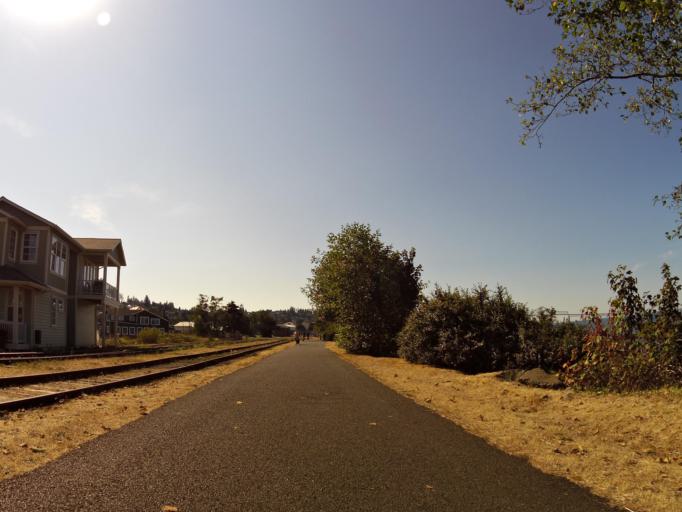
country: US
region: Oregon
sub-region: Clatsop County
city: Astoria
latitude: 46.1918
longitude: -123.8149
